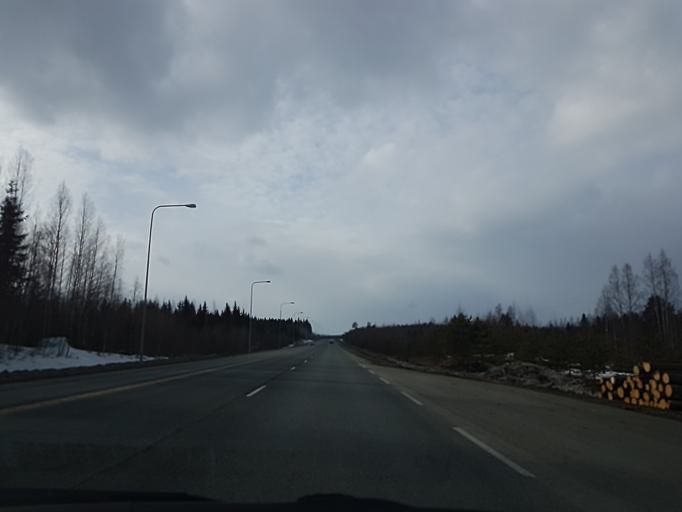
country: FI
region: Northern Savo
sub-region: Kuopio
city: Kuopio
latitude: 62.9765
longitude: 27.8047
